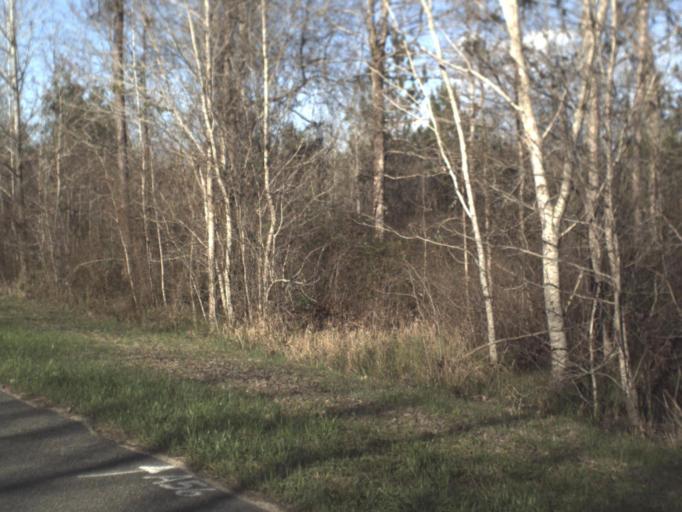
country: US
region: Florida
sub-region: Jackson County
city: Marianna
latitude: 30.6752
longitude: -85.2391
